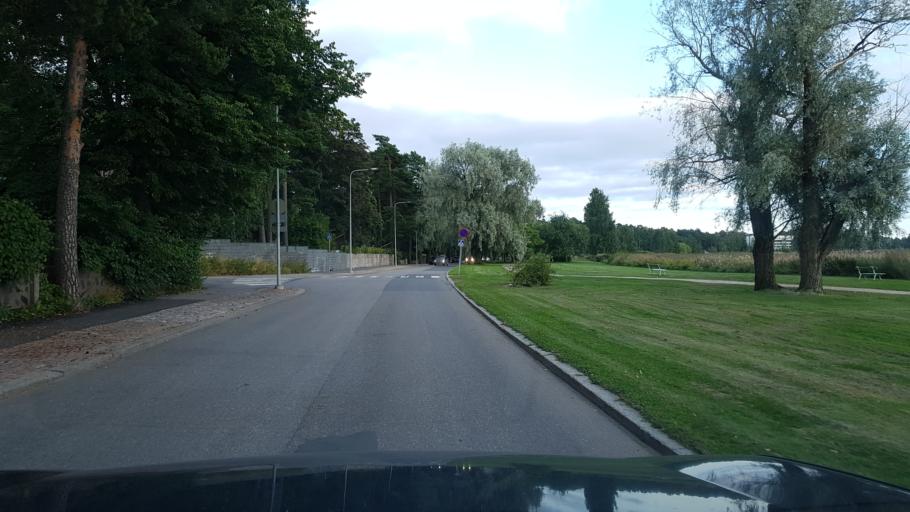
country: FI
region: Uusimaa
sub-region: Helsinki
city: Teekkarikylae
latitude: 60.1989
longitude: 24.8640
